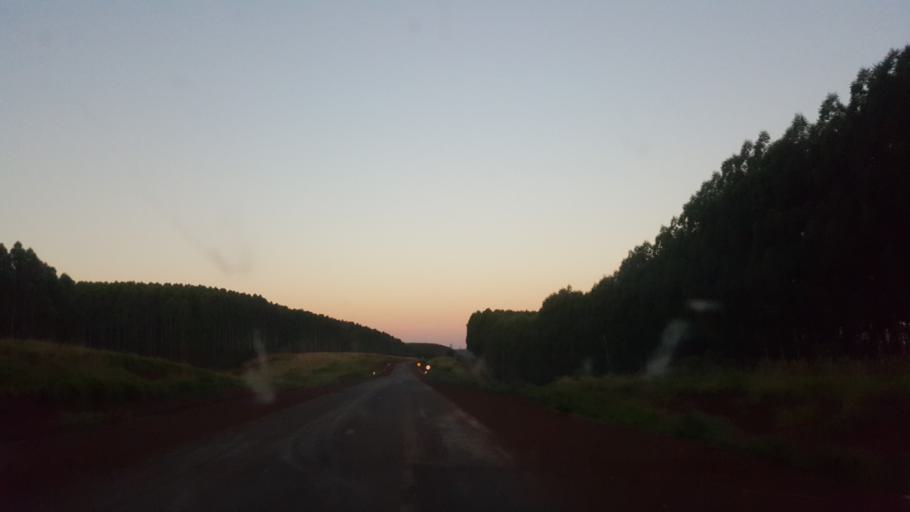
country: AR
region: Corrientes
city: Garruchos
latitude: -28.2500
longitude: -55.8457
